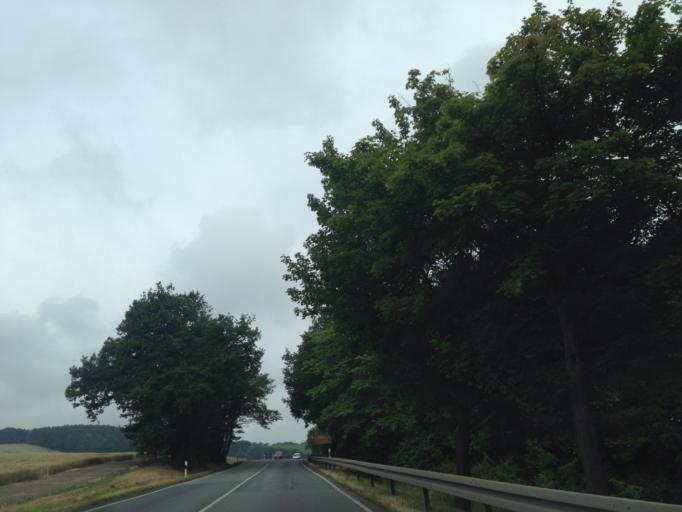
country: DE
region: Thuringia
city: Saalfeld
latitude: 50.6707
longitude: 11.3285
